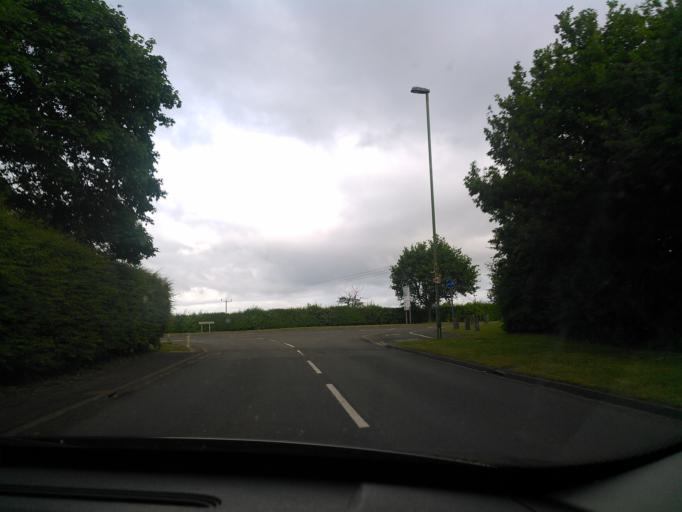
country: GB
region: England
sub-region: Shropshire
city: Shrewsbury
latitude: 52.7439
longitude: -2.7448
